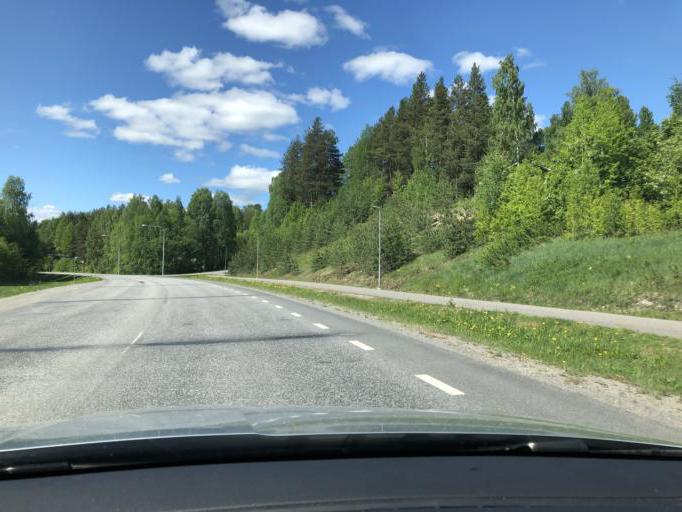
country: SE
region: Norrbotten
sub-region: Alvsbyns Kommun
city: AElvsbyn
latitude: 65.6673
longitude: 21.0253
